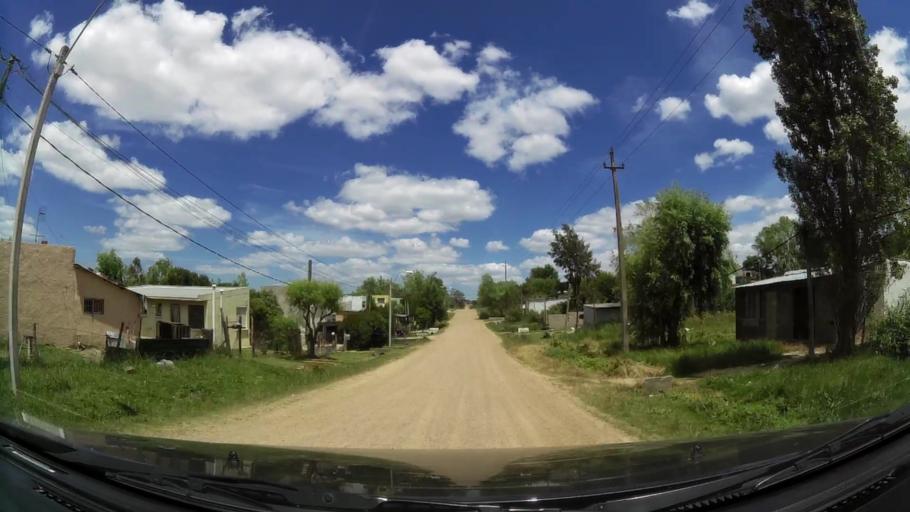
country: UY
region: Canelones
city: Colonia Nicolich
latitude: -34.8193
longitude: -55.9994
